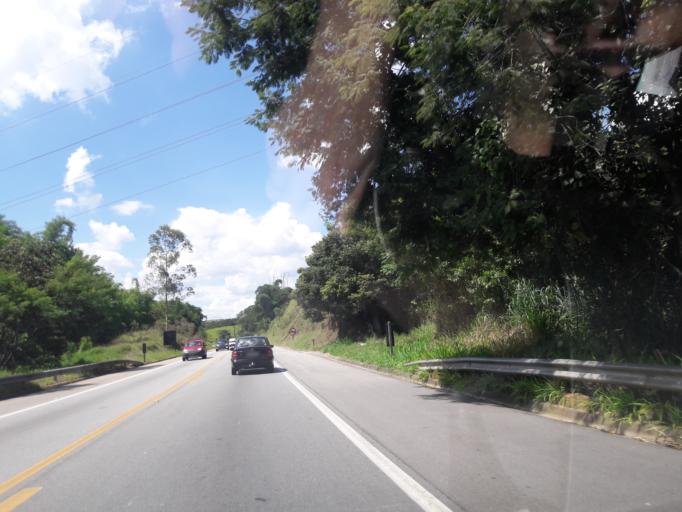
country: BR
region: Sao Paulo
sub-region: Cajamar
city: Cajamar
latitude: -23.3112
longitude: -46.8162
